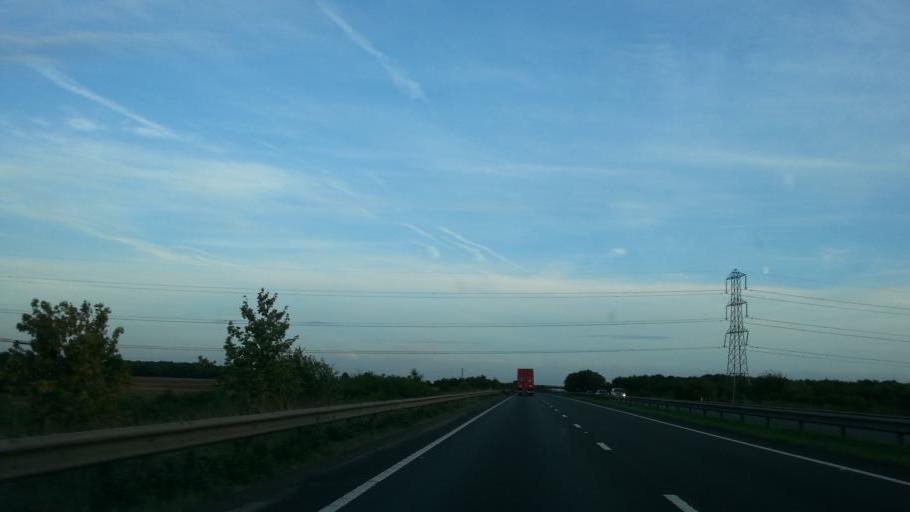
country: GB
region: England
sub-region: Nottinghamshire
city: Tuxford
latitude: 53.1945
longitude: -0.8428
